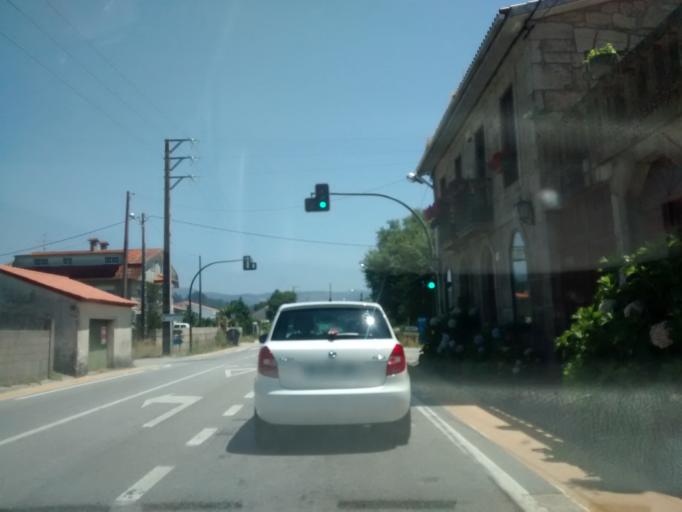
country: ES
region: Galicia
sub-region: Provincia de Pontevedra
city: Nigran
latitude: 42.1144
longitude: -8.7994
